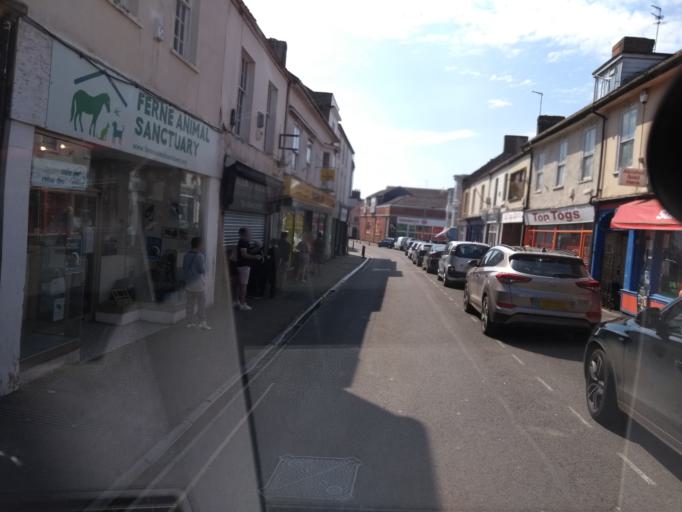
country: GB
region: England
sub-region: Somerset
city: Chard
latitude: 50.8724
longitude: -2.9656
